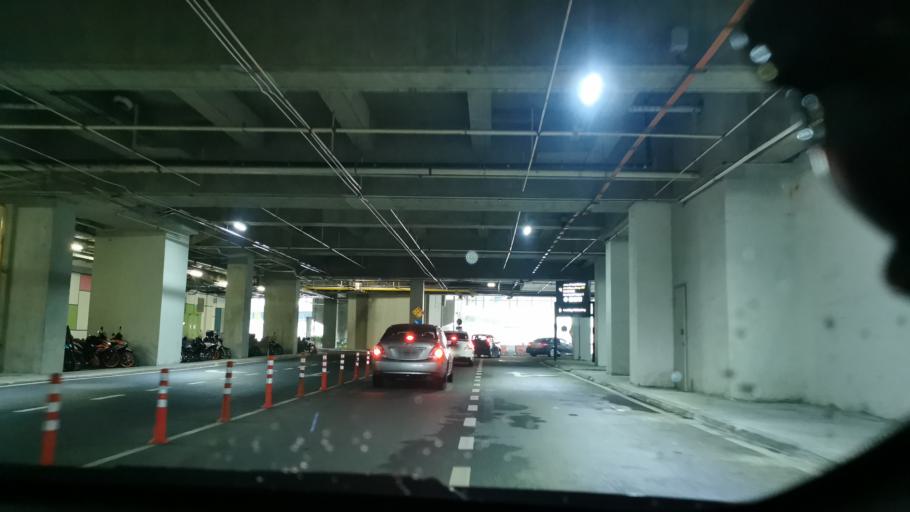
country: MY
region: Kuala Lumpur
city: Kuala Lumpur
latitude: 3.1183
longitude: 101.6737
